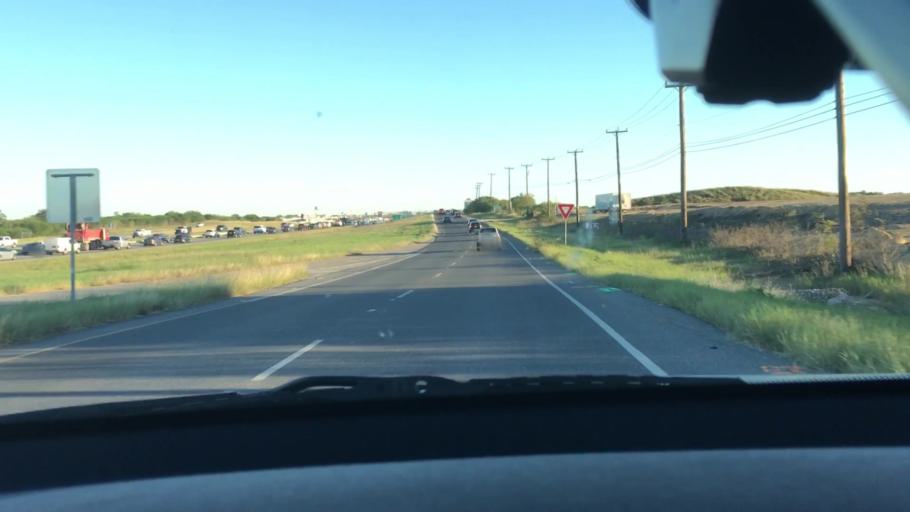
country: US
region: Texas
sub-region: Bexar County
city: Live Oak
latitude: 29.5892
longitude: -98.3510
